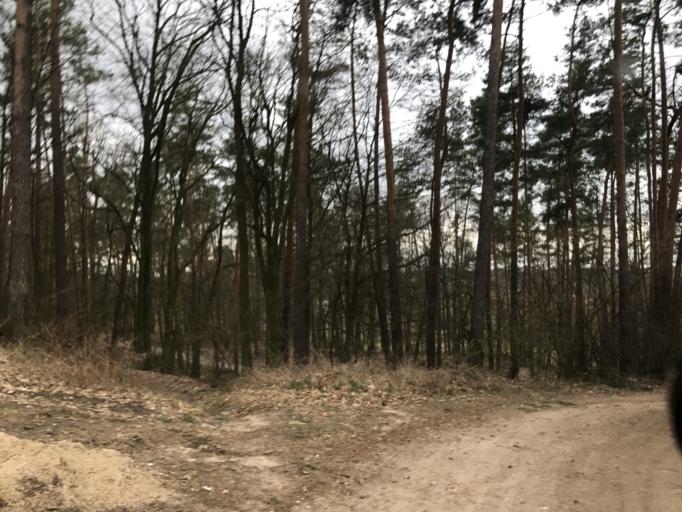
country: PL
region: Kujawsko-Pomorskie
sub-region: Powiat brodnicki
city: Gorzno
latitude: 53.2062
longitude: 19.6654
